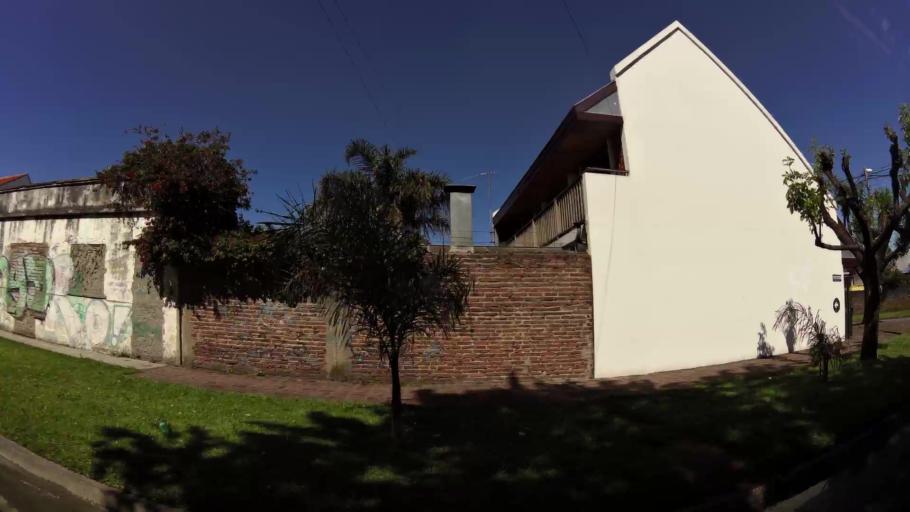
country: AR
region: Buenos Aires
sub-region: Partido de Quilmes
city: Quilmes
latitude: -34.6949
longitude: -58.3043
